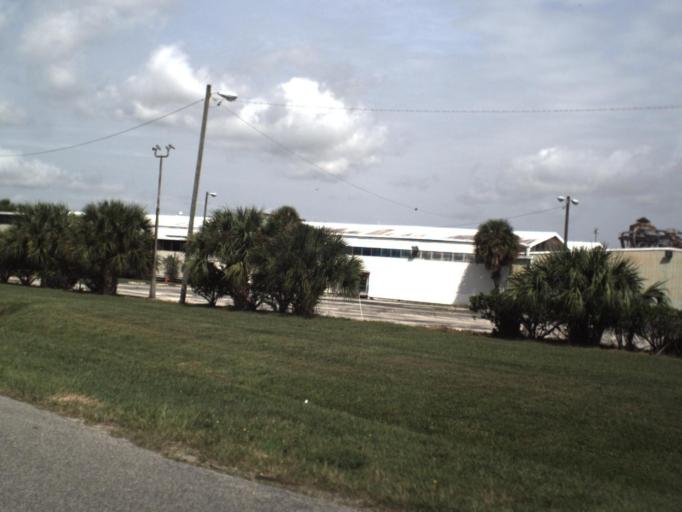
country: US
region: Florida
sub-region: Polk County
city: Auburndale
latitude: 28.0511
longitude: -81.7928
